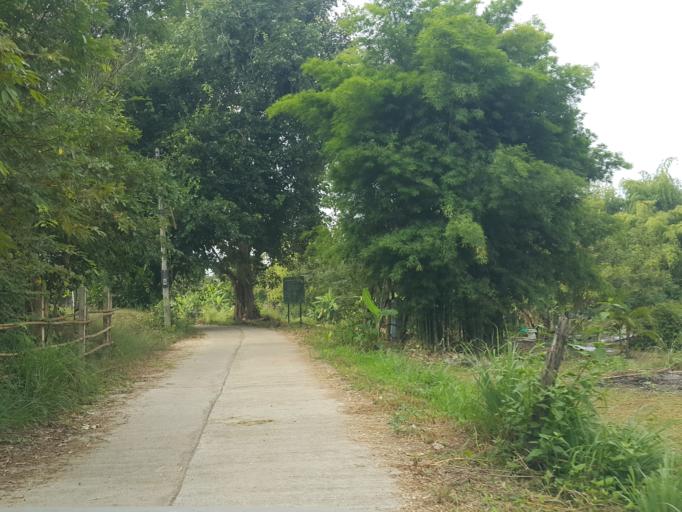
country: TH
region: Mae Hong Son
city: Wiang Nuea
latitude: 19.3732
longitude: 98.4469
